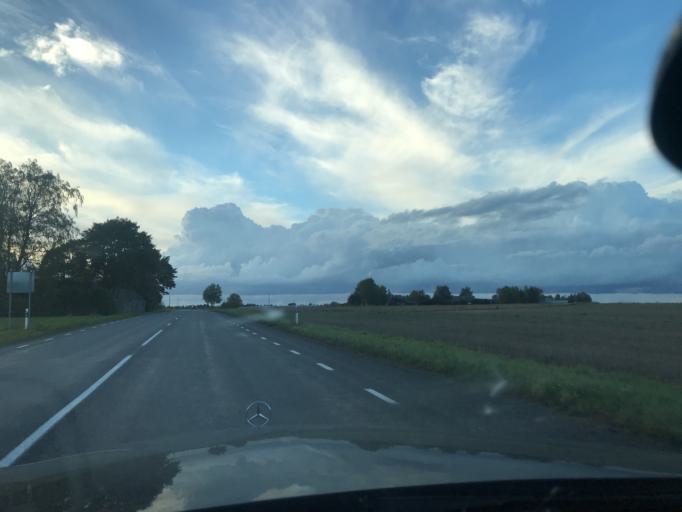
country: EE
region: Vorumaa
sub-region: Antsla vald
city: Vana-Antsla
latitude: 57.8857
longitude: 26.5232
